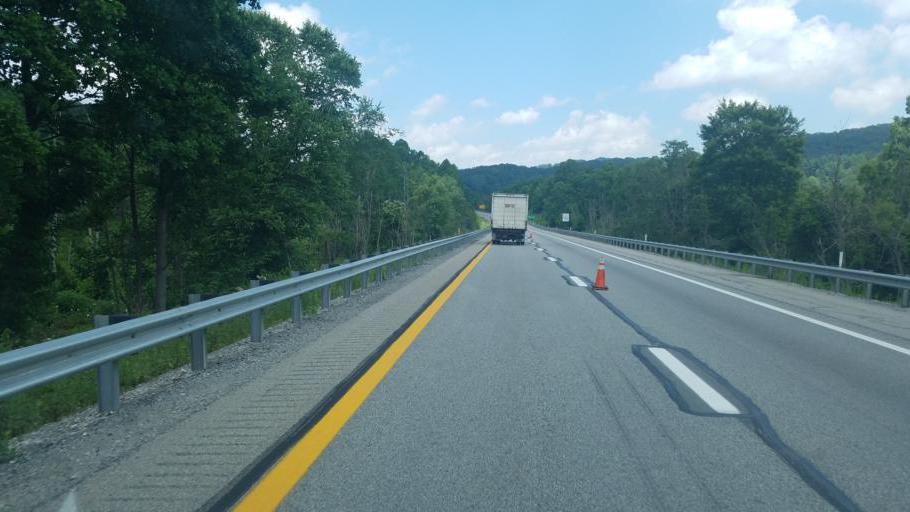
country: US
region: West Virginia
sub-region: Raleigh County
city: Bradley
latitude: 37.9225
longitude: -81.2678
